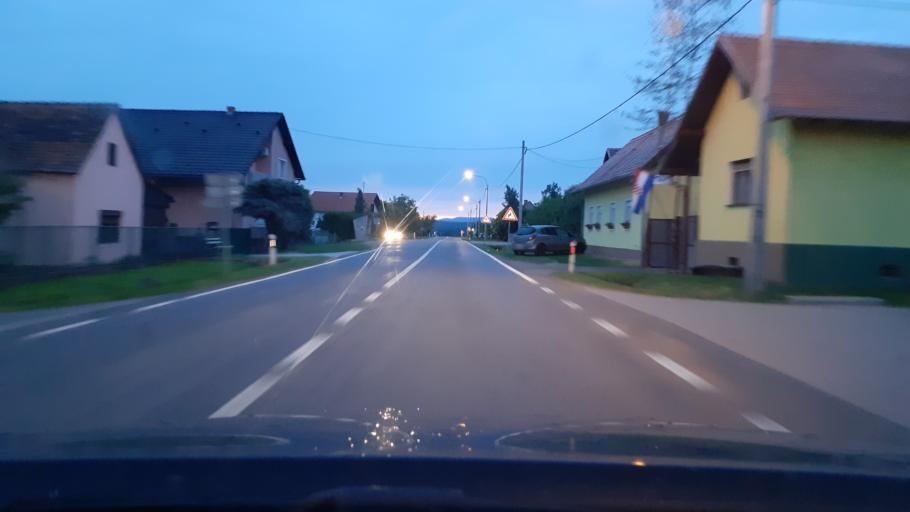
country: HR
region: Pozesko-Slavonska
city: Bilice
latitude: 45.2366
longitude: 17.8410
